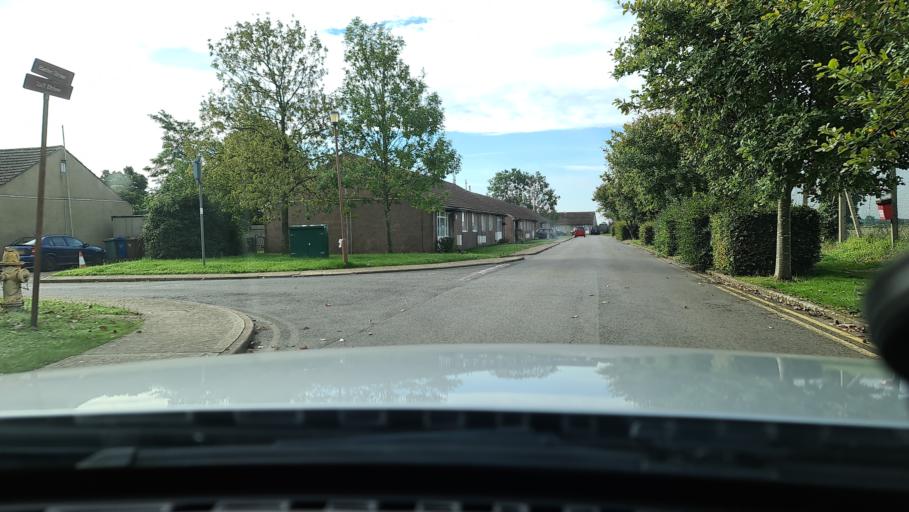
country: GB
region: England
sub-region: Oxfordshire
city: Somerton
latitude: 51.9252
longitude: -1.2610
